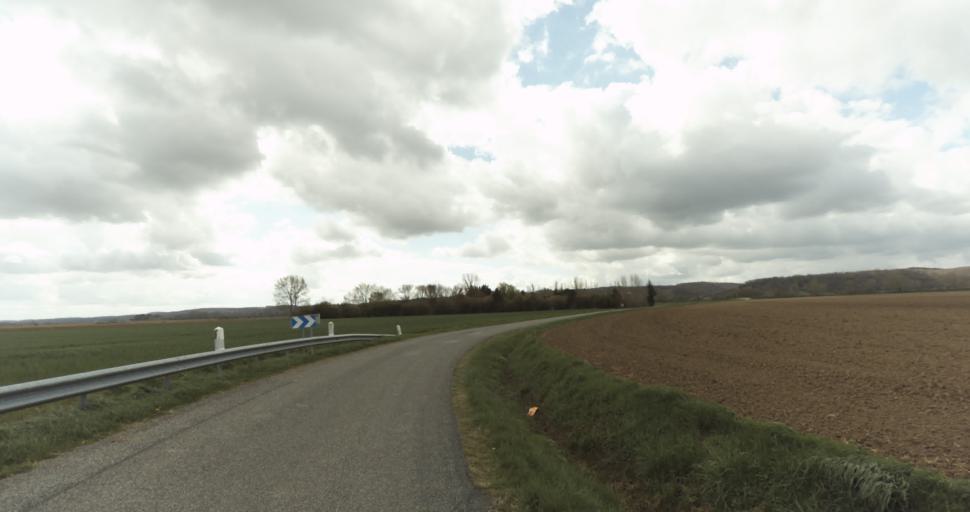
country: FR
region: Midi-Pyrenees
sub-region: Departement de la Haute-Garonne
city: Auterive
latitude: 43.3242
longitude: 1.4640
